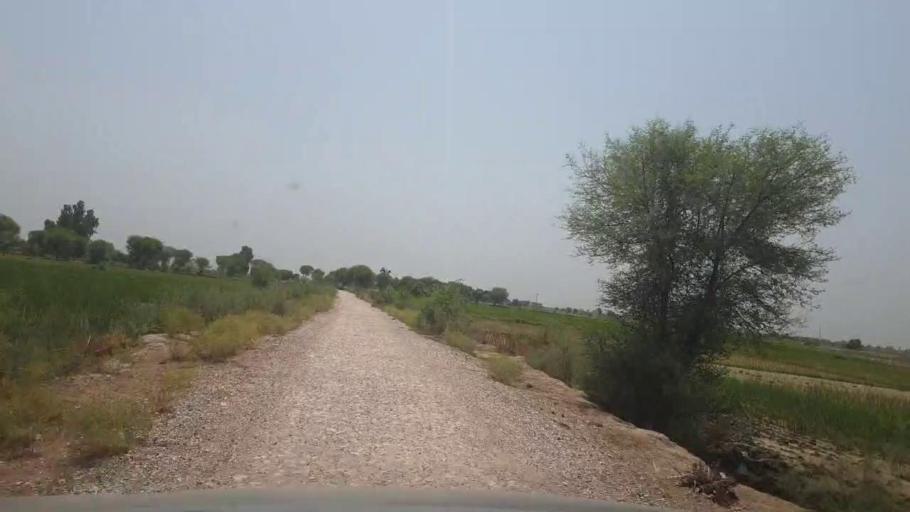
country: PK
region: Sindh
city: Lakhi
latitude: 27.8493
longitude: 68.6649
